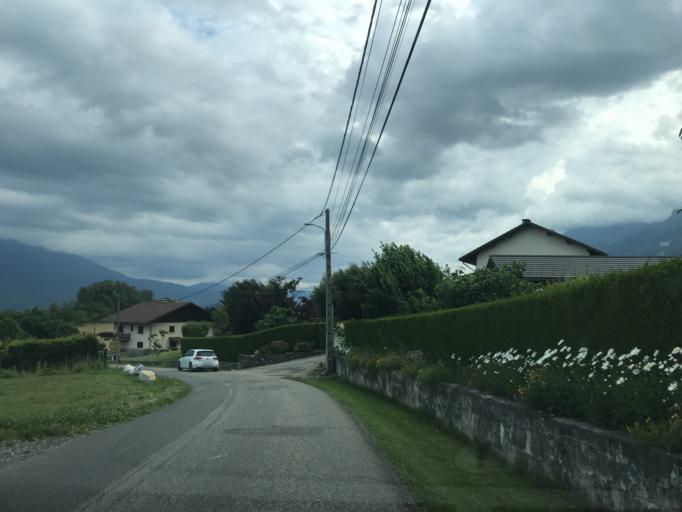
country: FR
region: Rhone-Alpes
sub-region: Departement de la Savoie
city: Mercury
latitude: 45.6797
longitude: 6.3409
